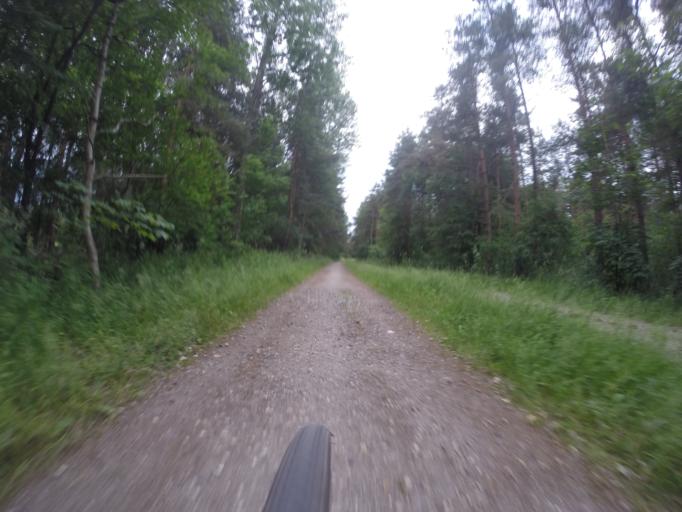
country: DK
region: Capital Region
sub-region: Ballerup Kommune
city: Ballerup
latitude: 55.7037
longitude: 12.3477
